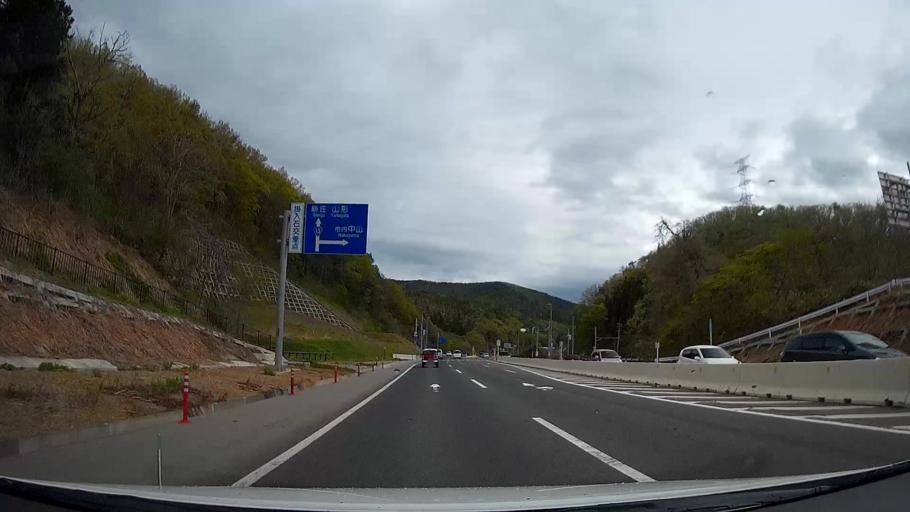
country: JP
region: Yamagata
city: Kaminoyama
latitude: 38.1276
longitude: 140.2186
